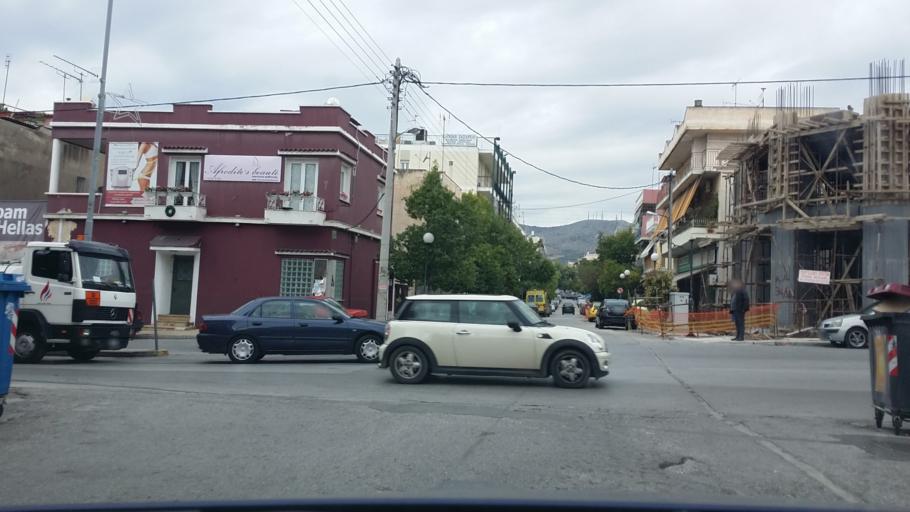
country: GR
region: Attica
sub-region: Nomarchia Athinas
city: Peristeri
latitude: 38.0124
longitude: 23.6890
